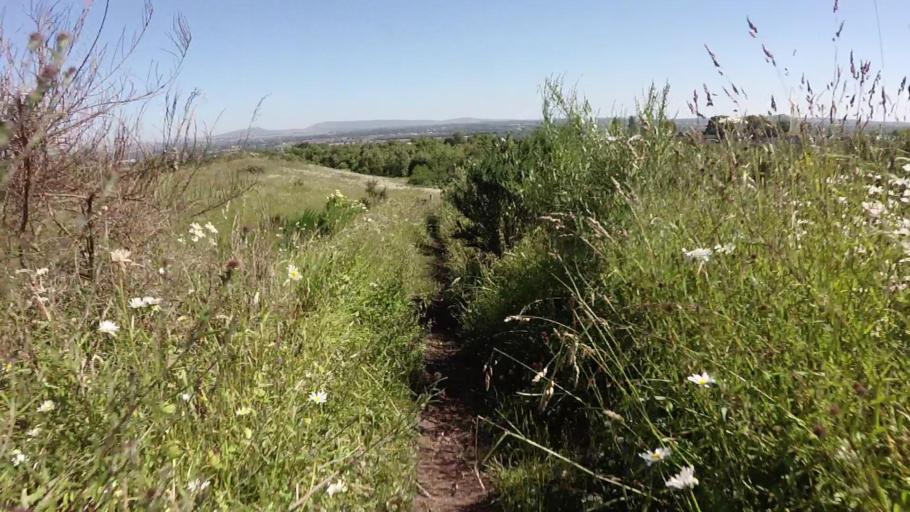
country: GB
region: Scotland
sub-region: West Lothian
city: West Calder
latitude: 55.8819
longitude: -3.5911
